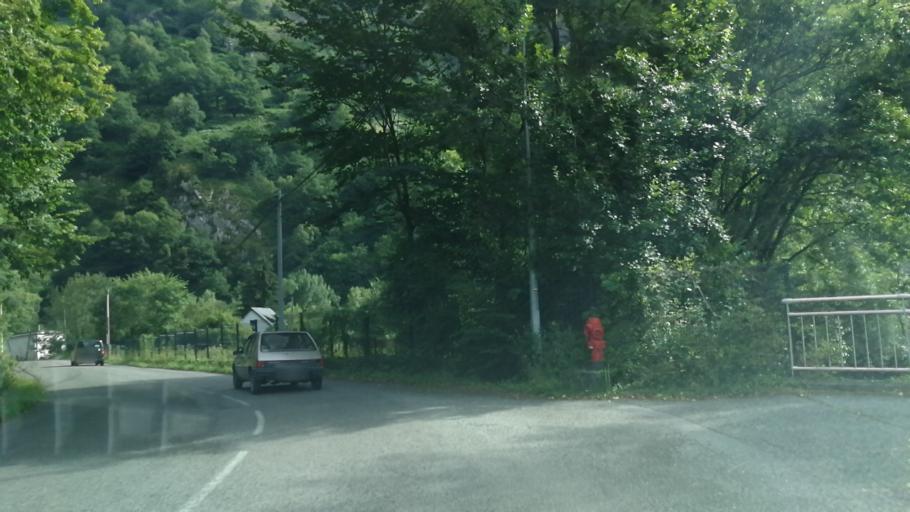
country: FR
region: Aquitaine
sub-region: Departement des Pyrenees-Atlantiques
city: Arette
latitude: 42.9441
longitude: -0.6117
